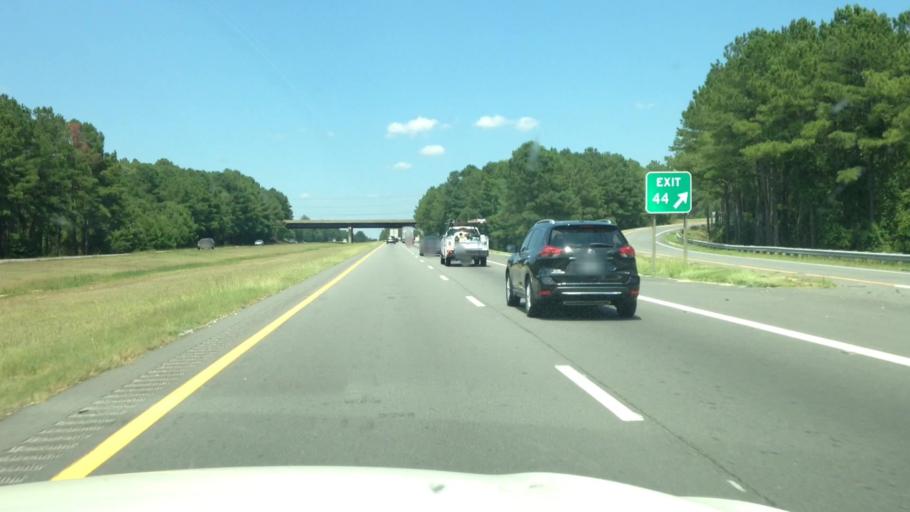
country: US
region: North Carolina
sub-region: Cumberland County
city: Hope Mills
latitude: 34.9595
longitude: -78.8921
